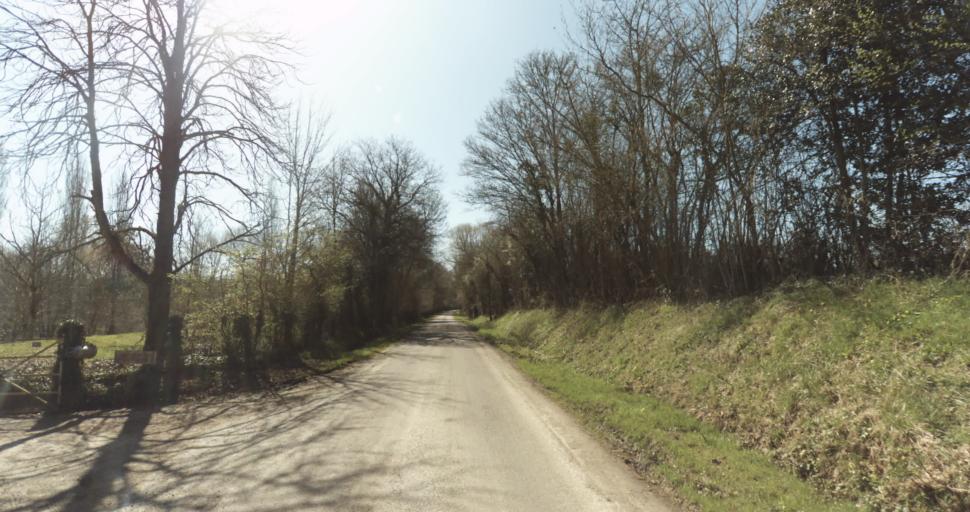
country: FR
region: Lower Normandy
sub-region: Departement du Calvados
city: Livarot
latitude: 49.0063
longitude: 0.0732
